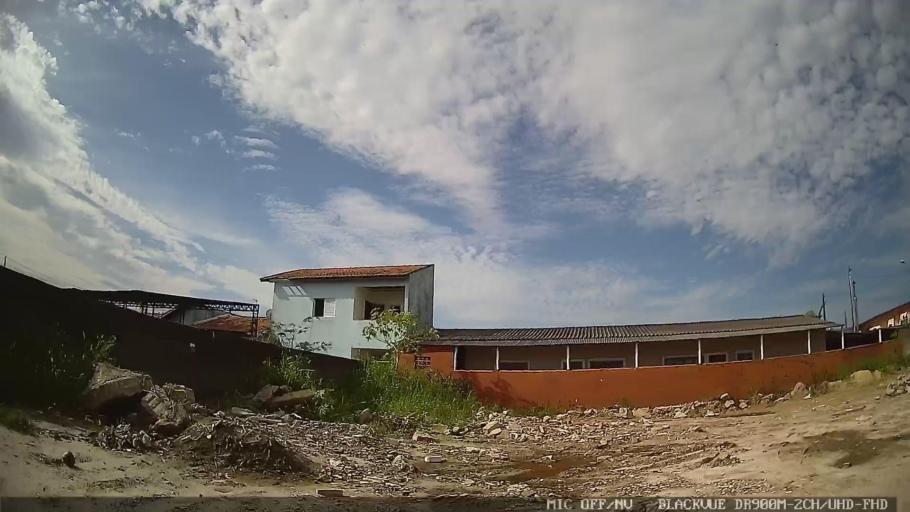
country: BR
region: Sao Paulo
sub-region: Itanhaem
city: Itanhaem
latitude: -24.1529
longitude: -46.7753
